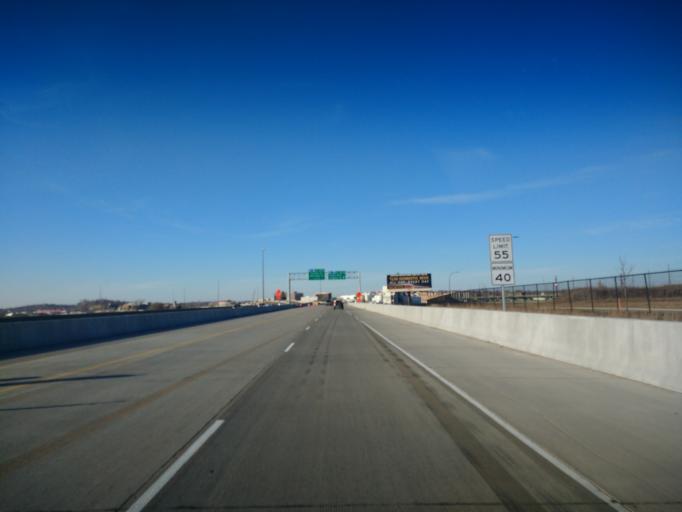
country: US
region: Iowa
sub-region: Woodbury County
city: Sioux City
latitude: 42.4818
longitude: -96.3892
